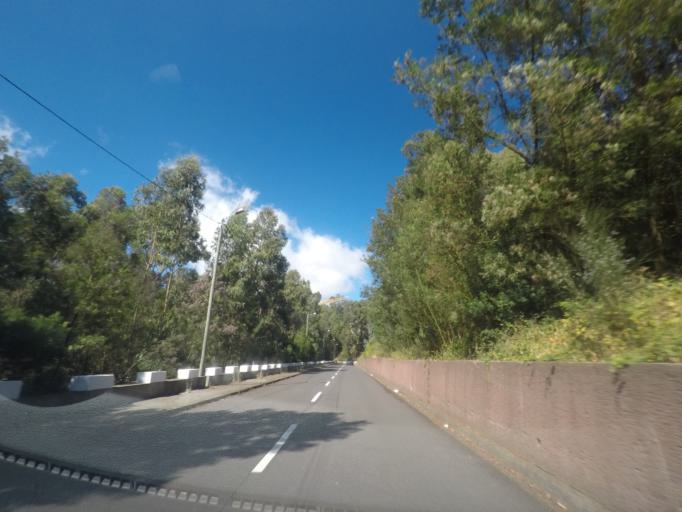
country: PT
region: Madeira
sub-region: Ribeira Brava
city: Campanario
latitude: 32.6830
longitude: -17.0415
